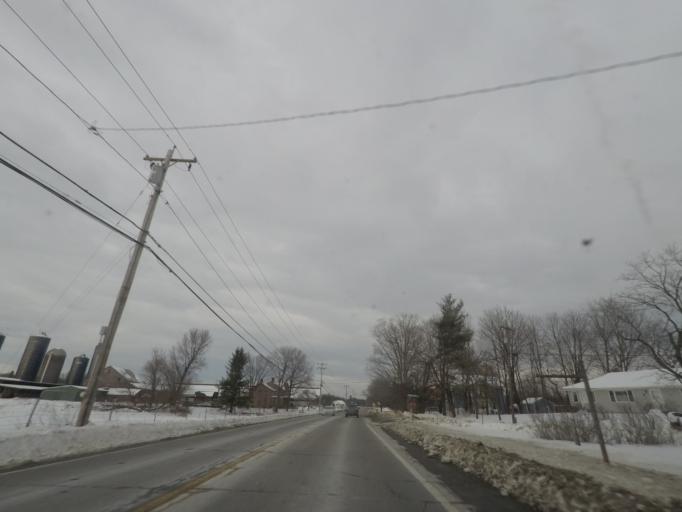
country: US
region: New York
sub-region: Columbia County
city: Kinderhook
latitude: 42.3824
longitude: -73.7223
